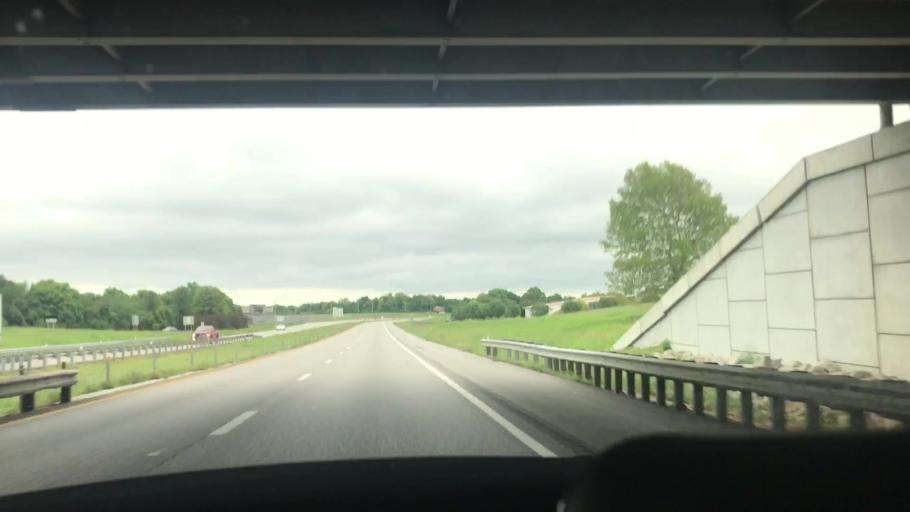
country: US
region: Missouri
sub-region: Greene County
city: Springfield
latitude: 37.2452
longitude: -93.3490
